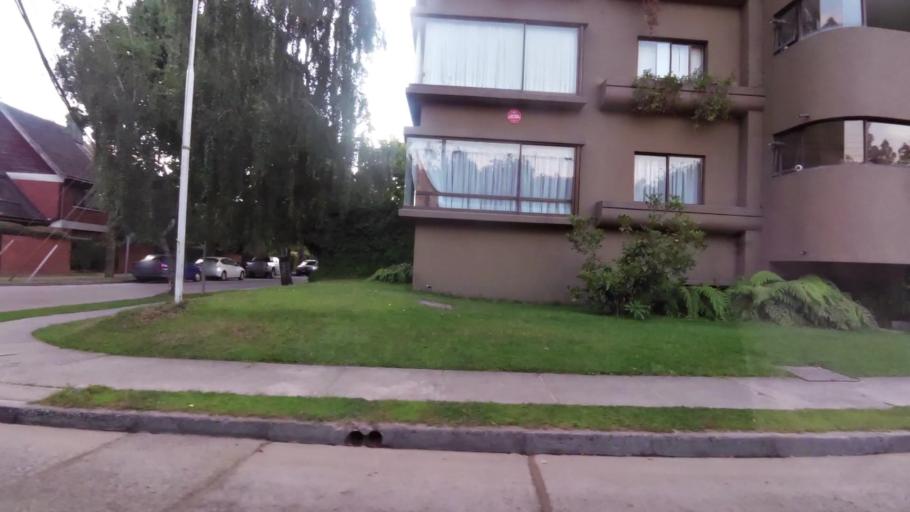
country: CL
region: Biobio
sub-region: Provincia de Concepcion
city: Concepcion
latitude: -36.8663
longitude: -73.0351
